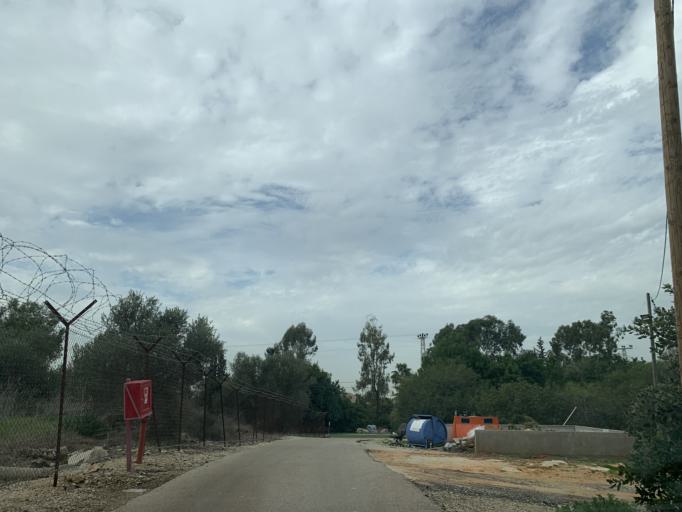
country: IL
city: Nirit
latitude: 32.1439
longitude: 34.9868
